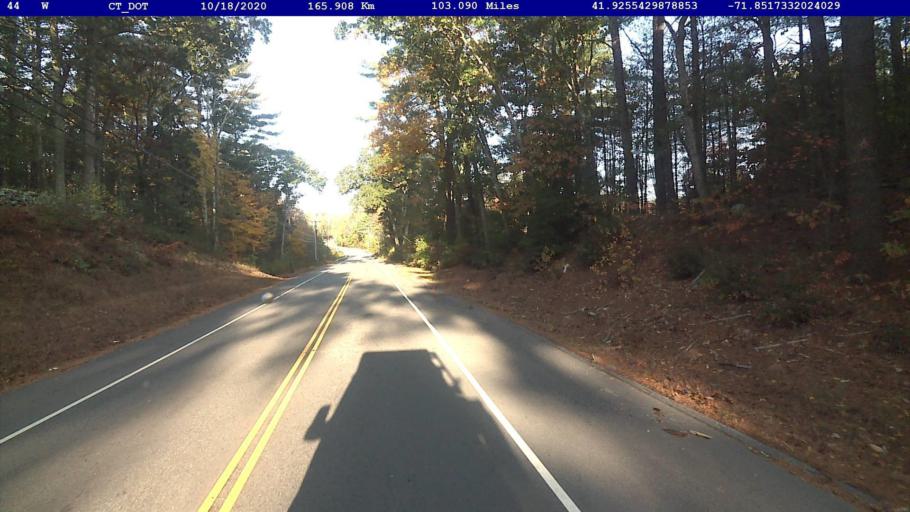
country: US
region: Connecticut
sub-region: Windham County
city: Thompson
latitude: 41.9257
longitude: -71.8517
